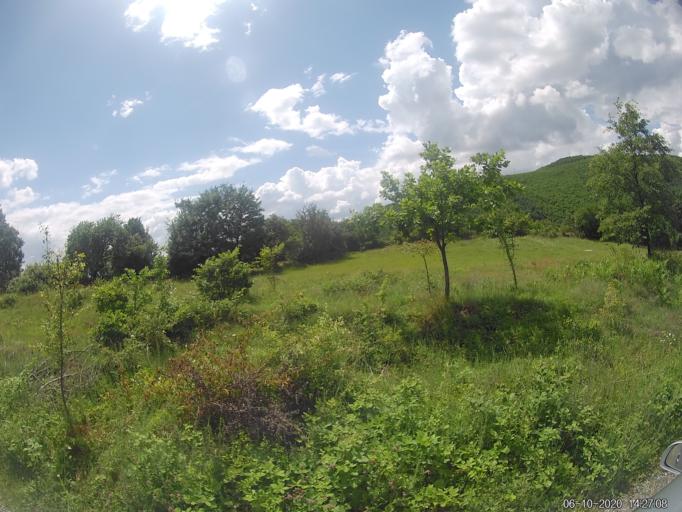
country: XK
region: Prizren
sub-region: Komuna e Therandes
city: Budakovo
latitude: 42.4101
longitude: 20.9148
